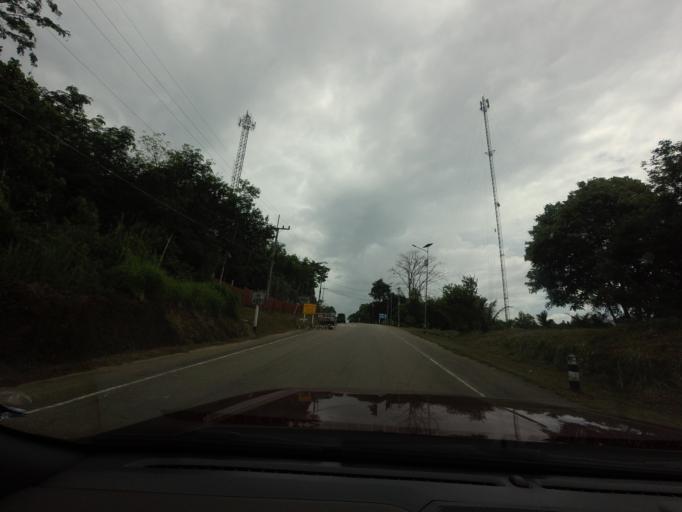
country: TH
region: Narathiwat
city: Sukhirin
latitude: 5.9779
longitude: 101.7070
